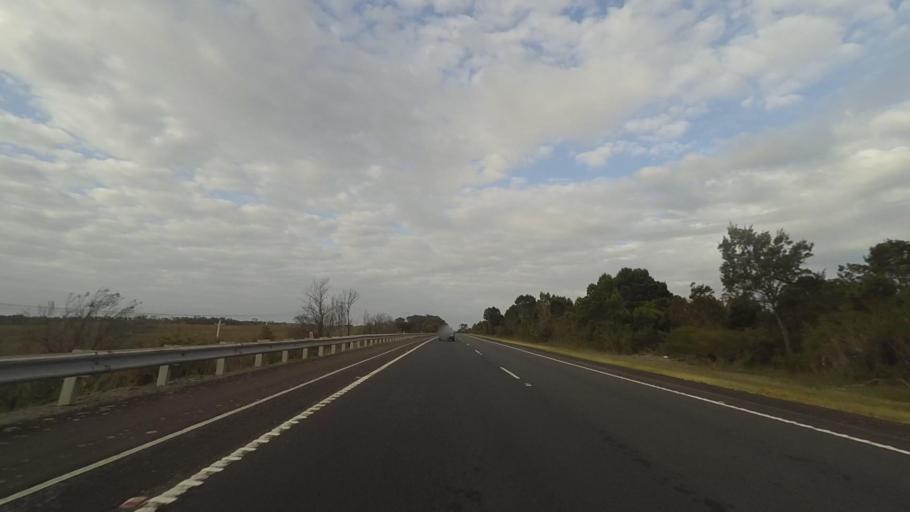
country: AU
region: New South Wales
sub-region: Wollongong
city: Bulli
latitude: -34.2629
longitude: 150.9282
